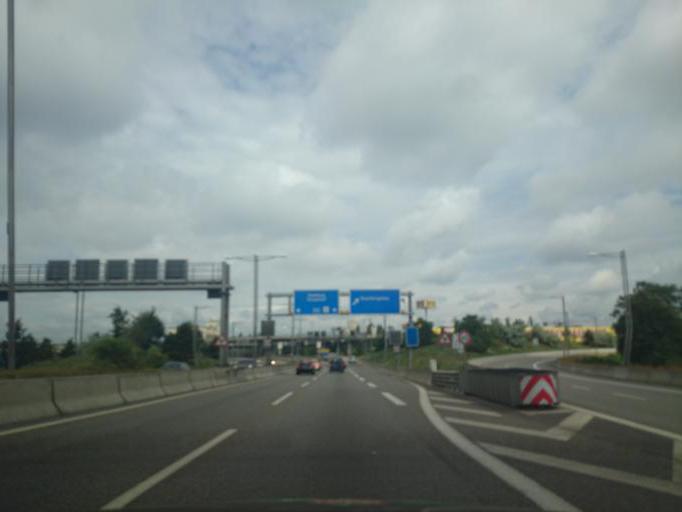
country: DE
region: Berlin
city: Plaenterwald
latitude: 52.4621
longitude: 13.4554
